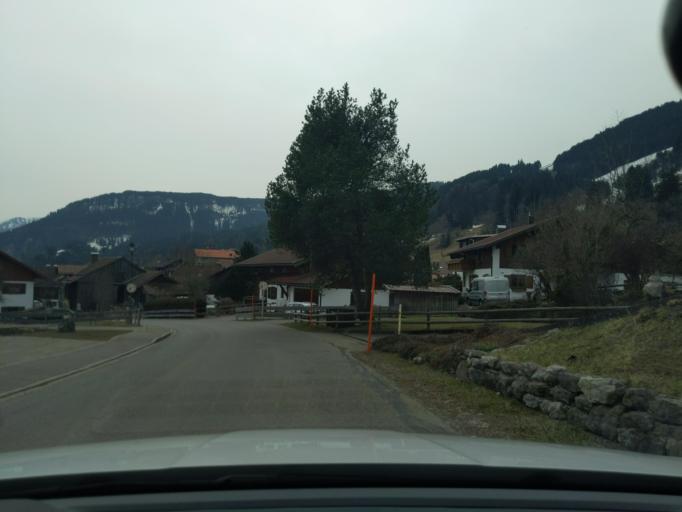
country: DE
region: Bavaria
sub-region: Swabia
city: Bolsterlang
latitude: 47.4621
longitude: 10.2321
